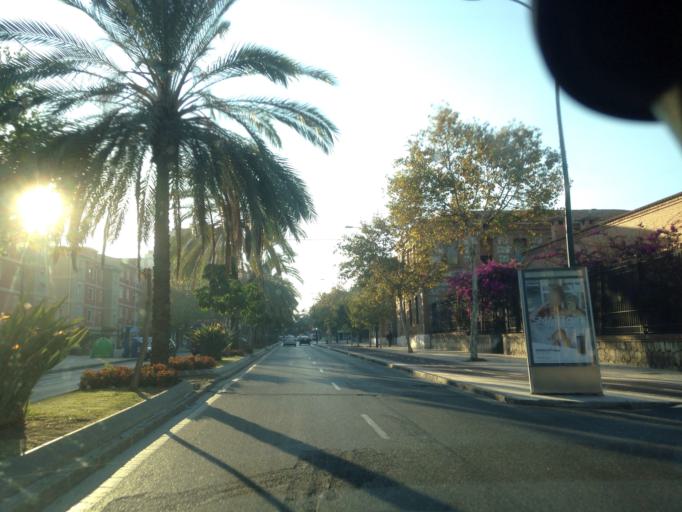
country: ES
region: Andalusia
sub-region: Provincia de Malaga
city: Malaga
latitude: 36.7118
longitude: -4.4438
